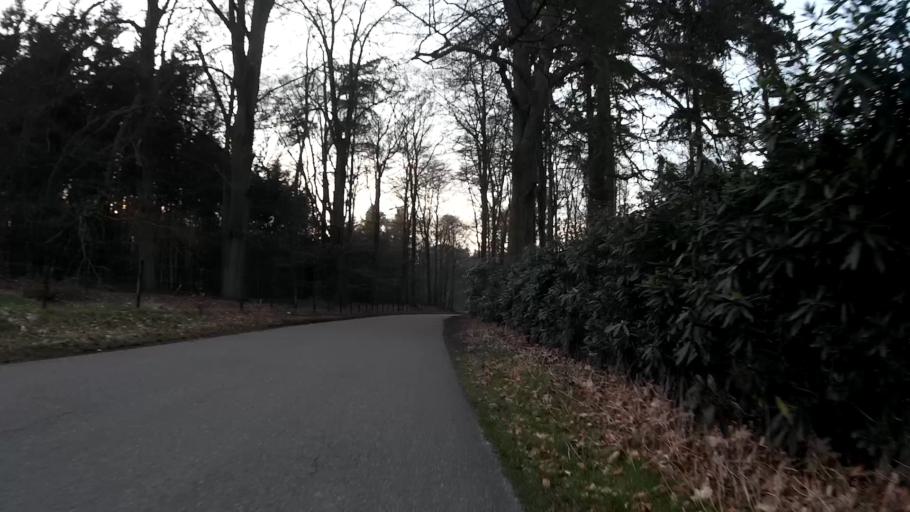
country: NL
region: Utrecht
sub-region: Gemeente Veenendaal
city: Veenendaal
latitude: 52.0080
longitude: 5.5313
